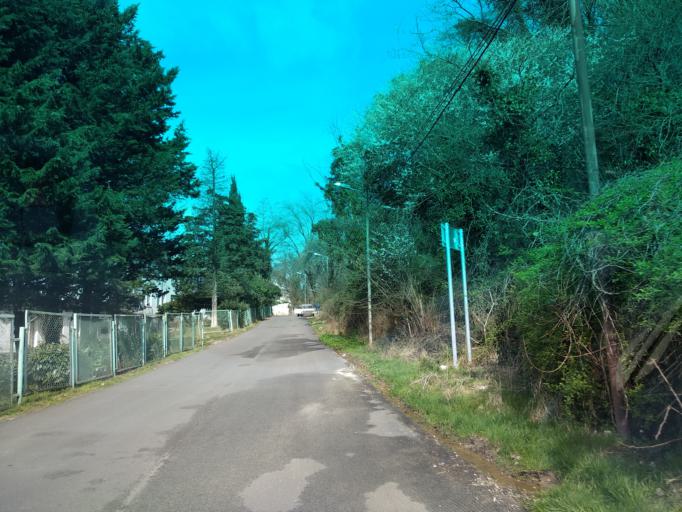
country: RU
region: Krasnodarskiy
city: Shepsi
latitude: 44.0343
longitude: 39.1477
